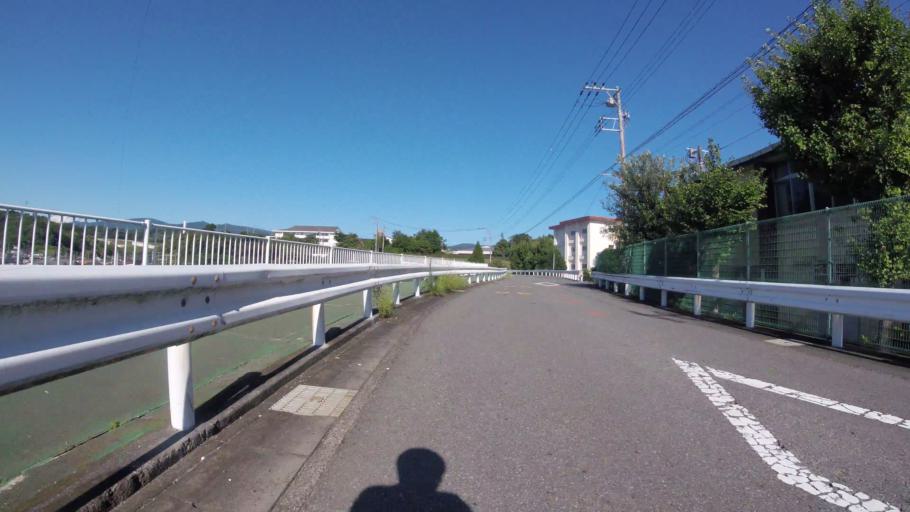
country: JP
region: Shizuoka
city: Mishima
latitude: 35.1334
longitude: 138.9333
